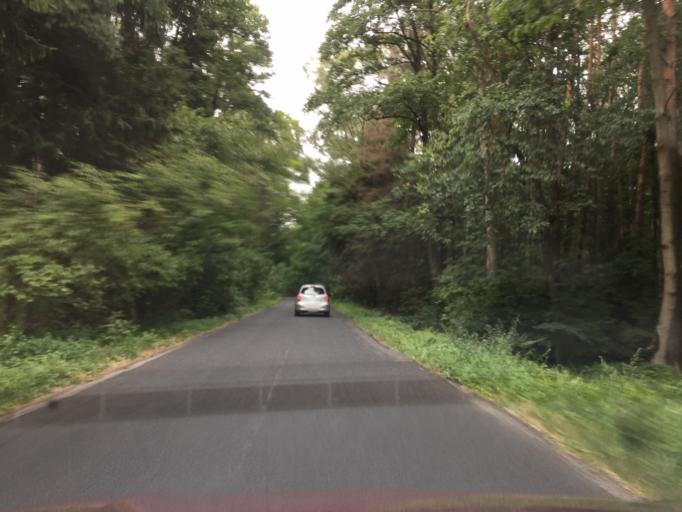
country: PL
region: Greater Poland Voivodeship
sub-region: Powiat kaliski
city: Stawiszyn
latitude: 51.9670
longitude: 18.1798
